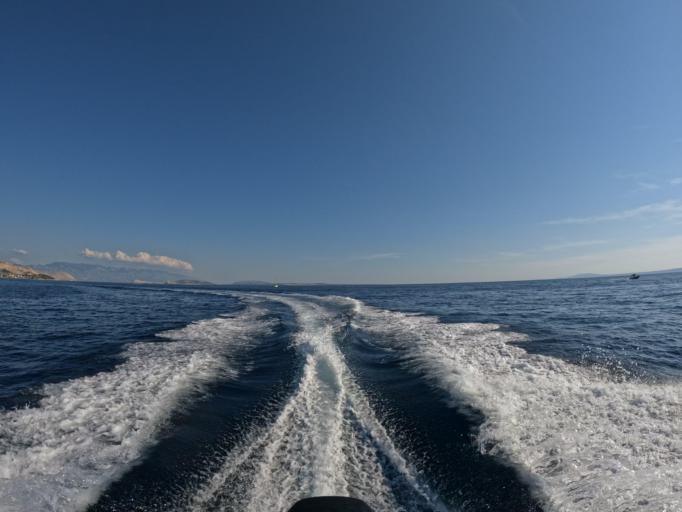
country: HR
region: Primorsko-Goranska
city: Punat
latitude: 44.9647
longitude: 14.6482
